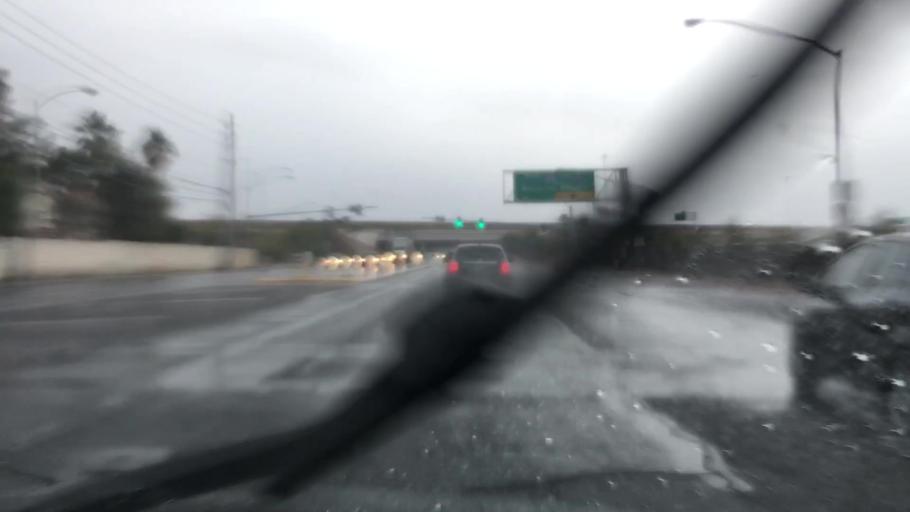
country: US
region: Nevada
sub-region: Clark County
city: Paradise
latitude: 36.0575
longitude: -115.1365
